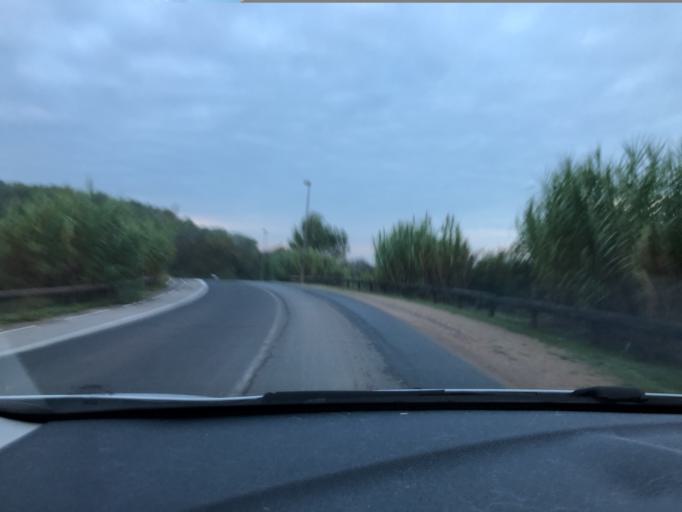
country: FR
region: Languedoc-Roussillon
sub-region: Departement de l'Herault
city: Montferrier-sur-Lez
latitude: 43.6777
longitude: 3.8725
